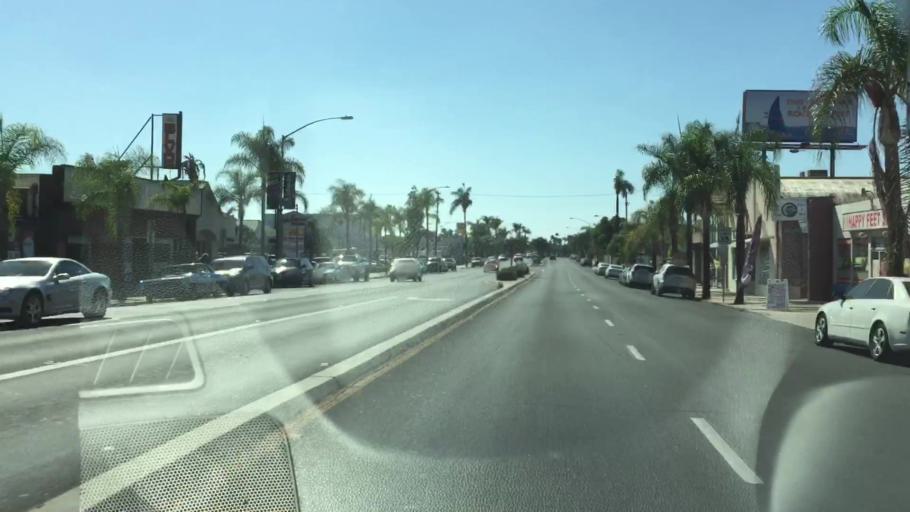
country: US
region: California
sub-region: San Diego County
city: La Mesa
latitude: 32.7687
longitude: -117.0478
